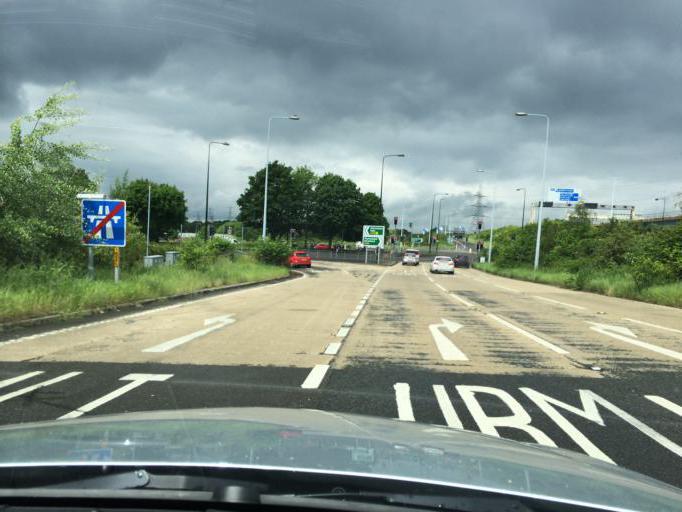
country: GB
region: England
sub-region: Trafford
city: Stretford
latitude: 53.4358
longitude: -2.3141
